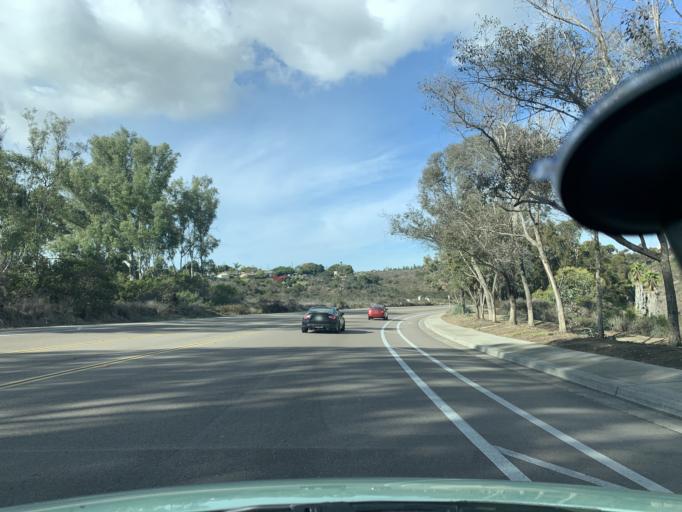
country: US
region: California
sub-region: San Diego County
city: San Diego
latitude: 32.7943
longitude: -117.1708
